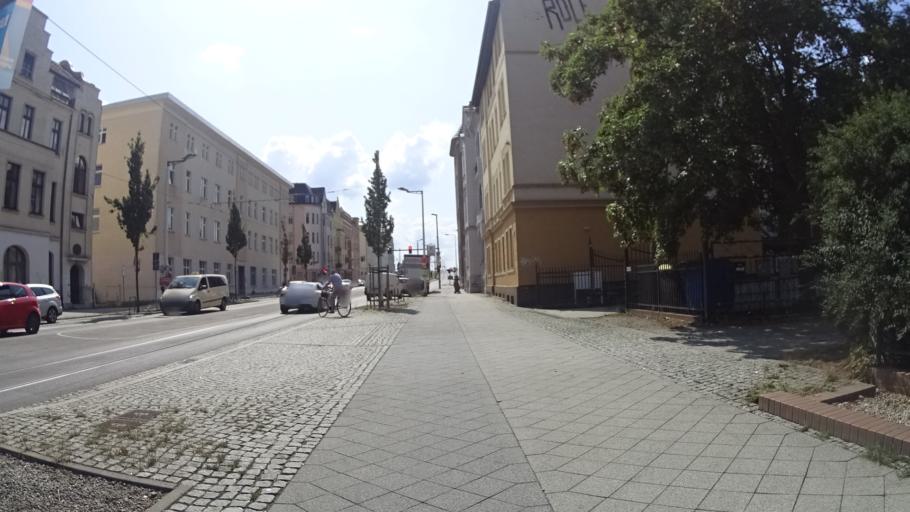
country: DE
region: Brandenburg
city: Cottbus
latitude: 51.7550
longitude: 14.3282
